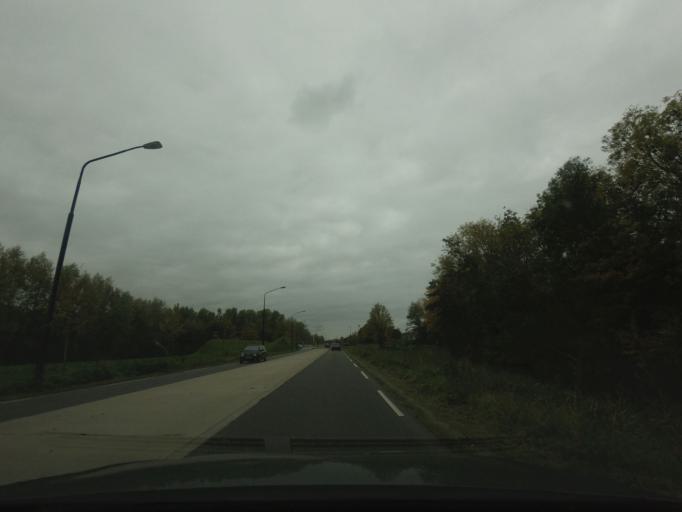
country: NL
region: North Holland
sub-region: Gemeente Heerhugowaard
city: Heerhugowaard
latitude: 52.6637
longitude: 4.8520
